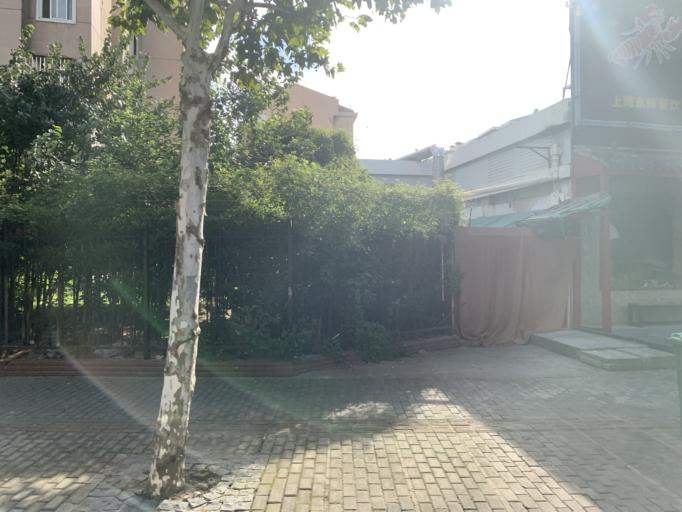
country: CN
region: Shanghai Shi
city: Huamu
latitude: 31.2028
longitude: 121.5404
